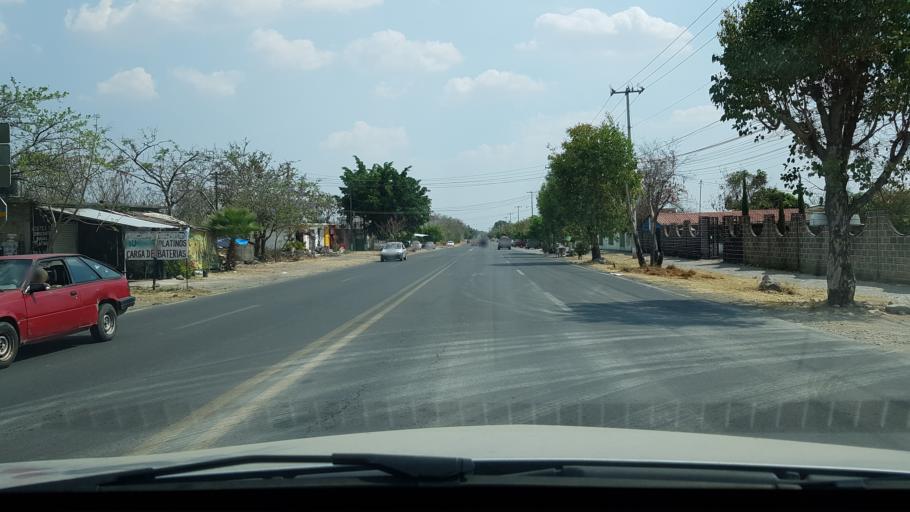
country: MX
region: Morelos
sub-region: Temoac
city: Temoac
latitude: 18.7657
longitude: -98.7792
